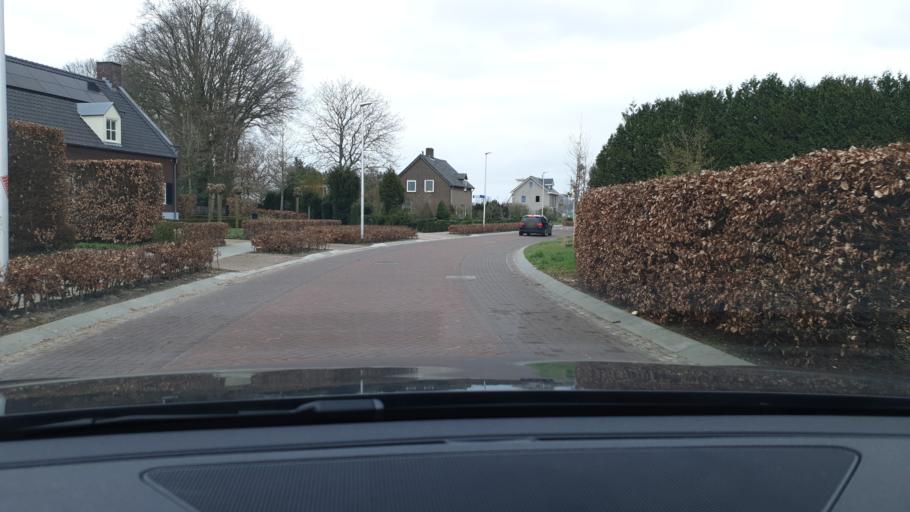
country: NL
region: North Brabant
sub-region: Gemeente Veldhoven
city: Oerle
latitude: 51.4164
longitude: 5.3583
